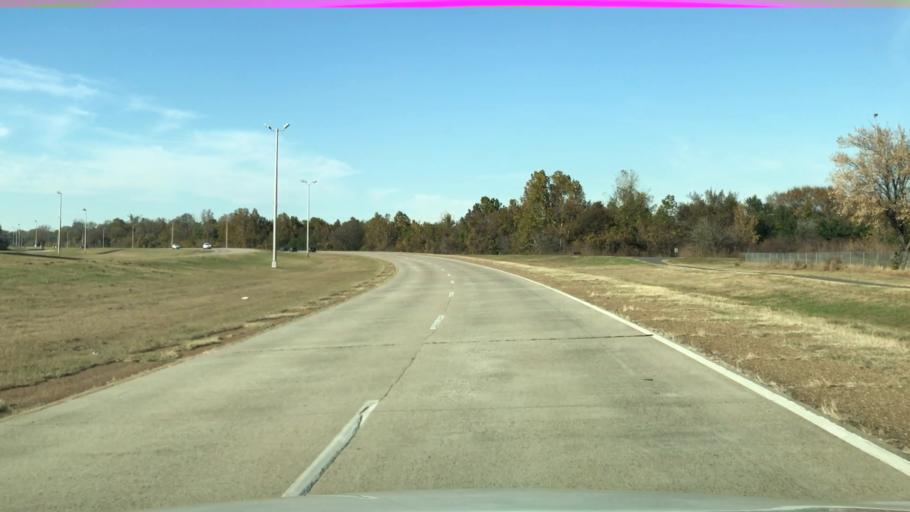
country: US
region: Louisiana
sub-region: Bossier Parish
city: Bossier City
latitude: 32.4828
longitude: -93.6933
